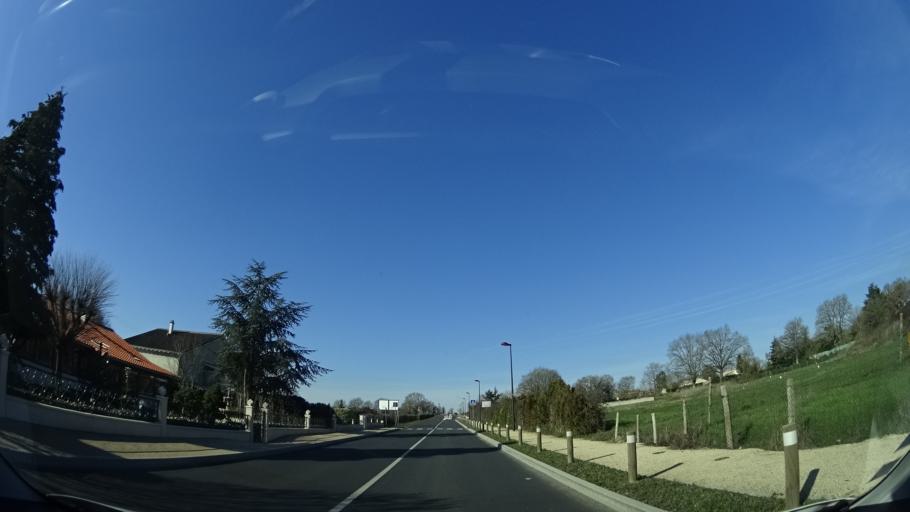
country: FR
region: Poitou-Charentes
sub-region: Departement des Deux-Sevres
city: Chiche
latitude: 46.8315
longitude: -0.3599
